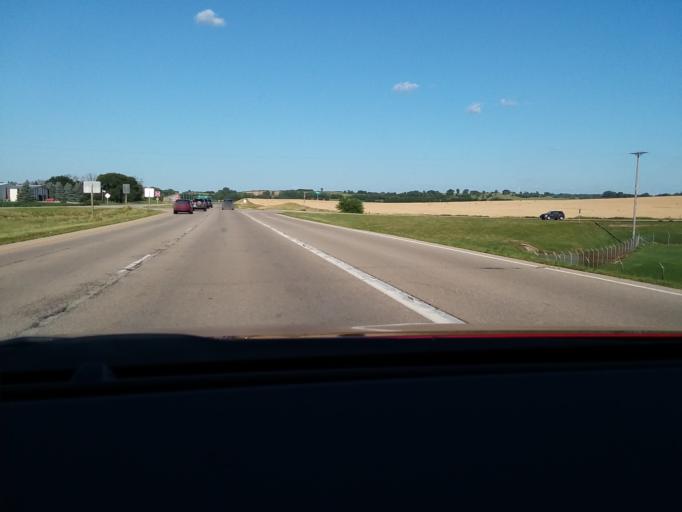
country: US
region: Wisconsin
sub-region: Dane County
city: Waunakee
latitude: 43.1916
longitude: -89.4230
